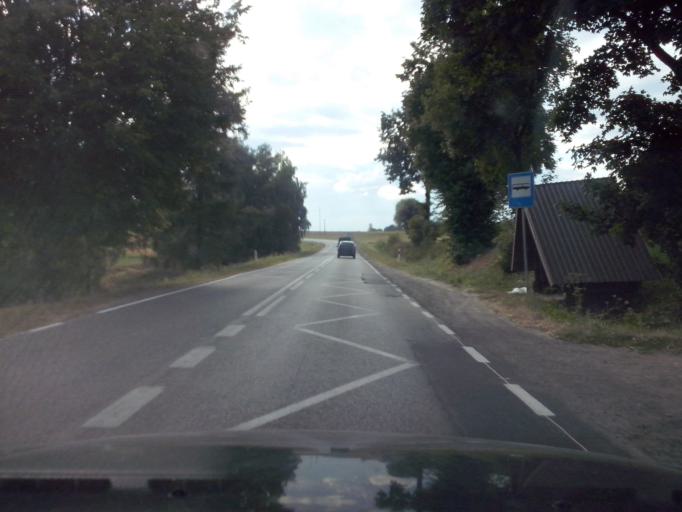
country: PL
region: Swietokrzyskie
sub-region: Powiat kielecki
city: Lagow
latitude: 50.7511
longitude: 21.0787
